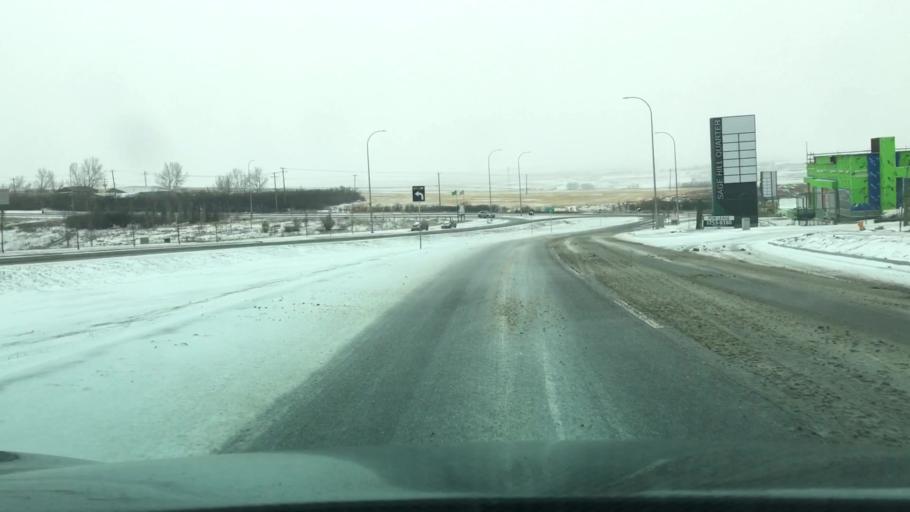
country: CA
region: Alberta
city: Calgary
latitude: 51.1811
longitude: -114.1606
